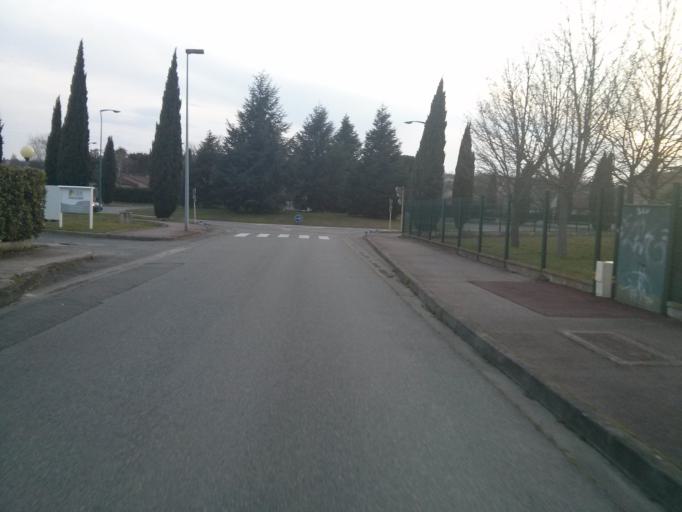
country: FR
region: Midi-Pyrenees
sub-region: Departement de la Haute-Garonne
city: Castanet-Tolosan
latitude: 43.5256
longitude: 1.5005
